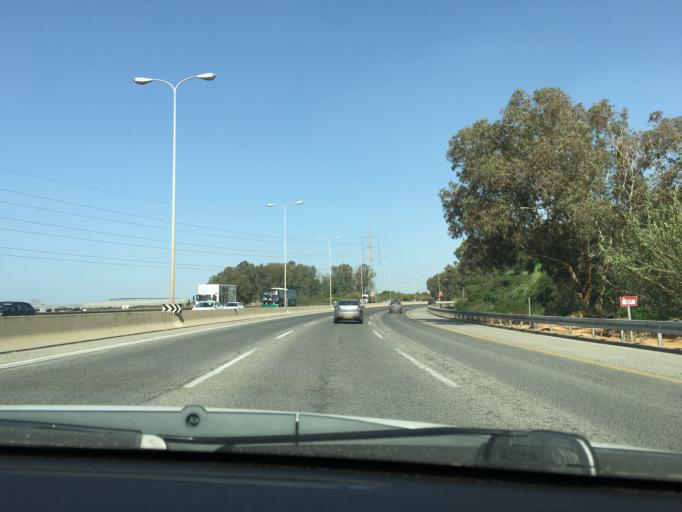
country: IL
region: Central District
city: Hod HaSharon
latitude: 32.1543
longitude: 34.8726
